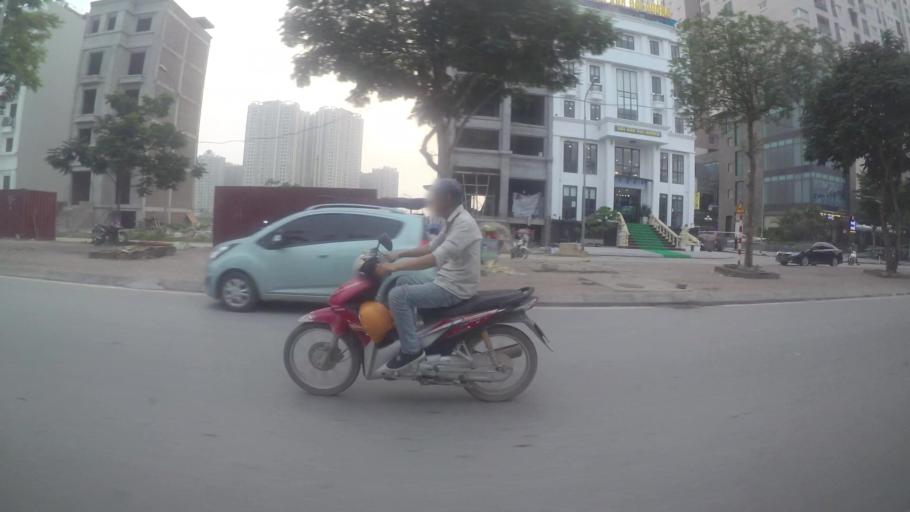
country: VN
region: Ha Noi
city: Cau Dien
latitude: 21.0078
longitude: 105.7313
